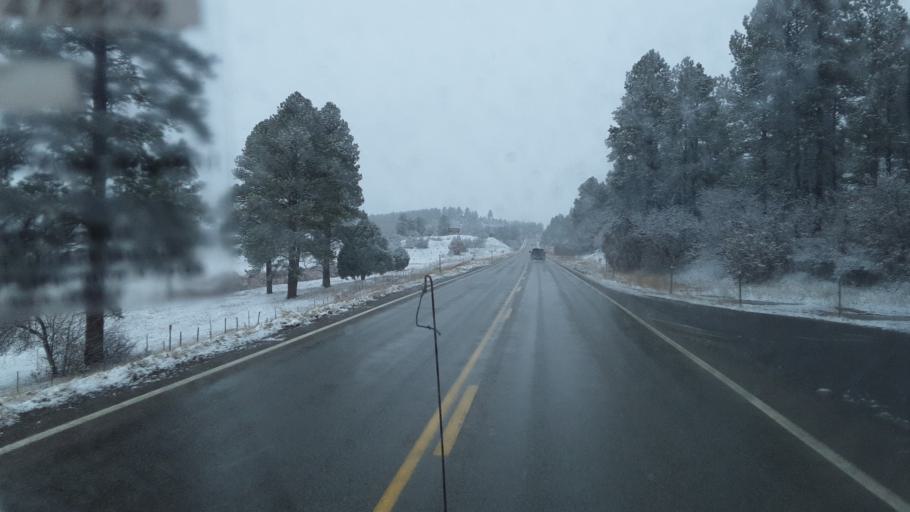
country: US
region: Colorado
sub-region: Archuleta County
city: Pagosa Springs
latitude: 37.2039
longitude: -106.9667
